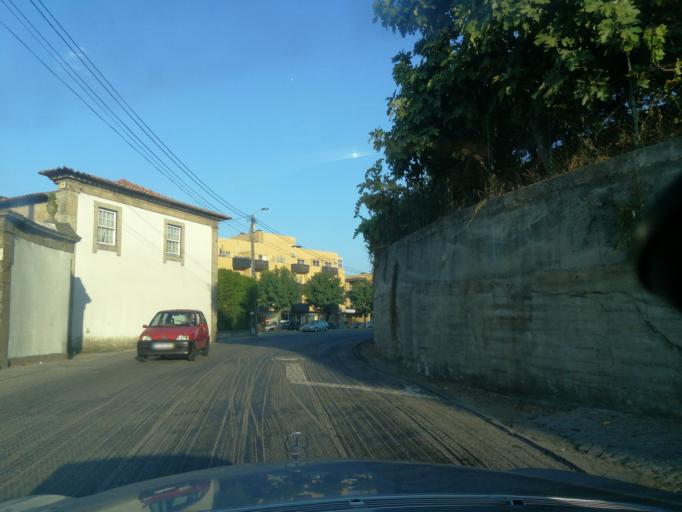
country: PT
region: Braga
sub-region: Braga
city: Braga
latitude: 41.5320
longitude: -8.4290
